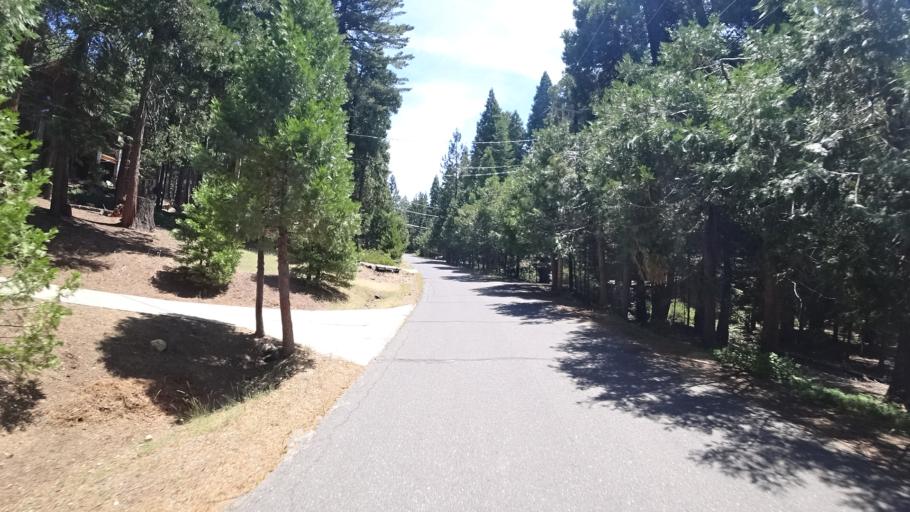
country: US
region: California
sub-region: Calaveras County
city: Arnold
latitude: 38.3185
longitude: -120.2547
